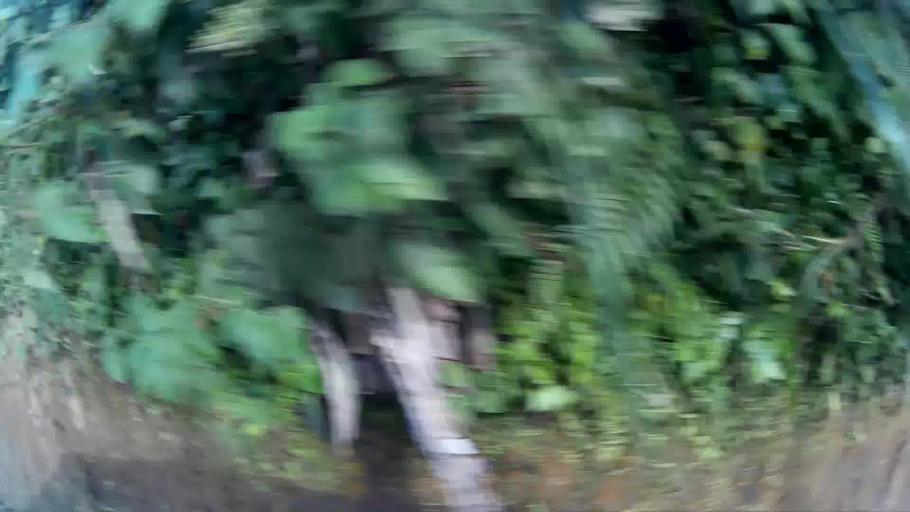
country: CO
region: Valle del Cauca
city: Ulloa
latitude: 4.7250
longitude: -75.6967
